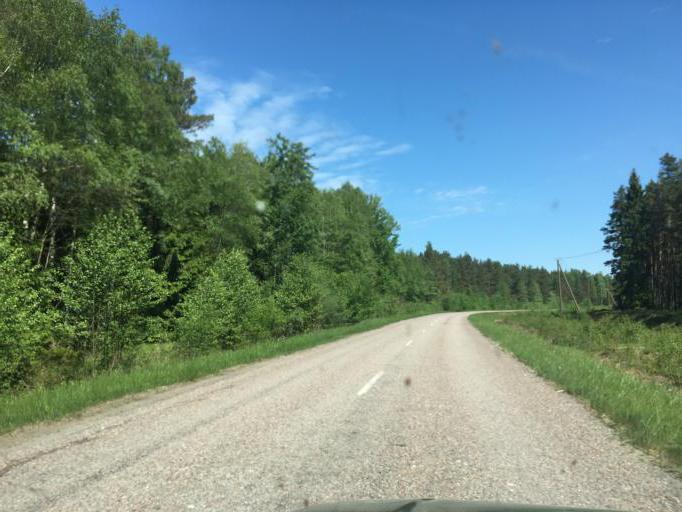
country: LV
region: Ventspils
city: Ventspils
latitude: 57.4633
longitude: 21.6534
